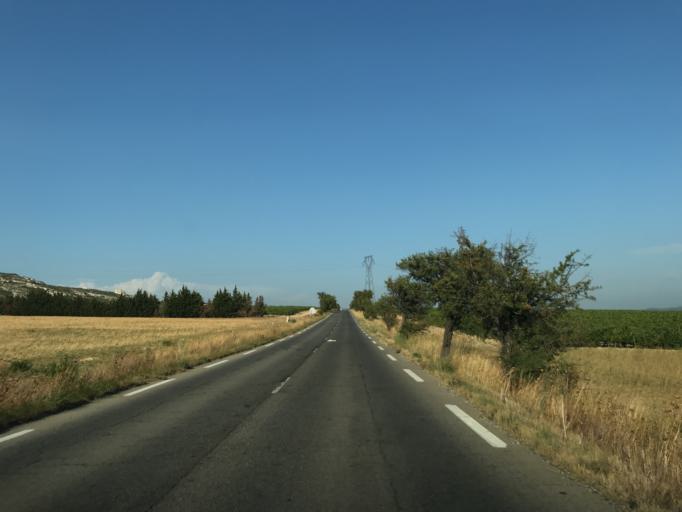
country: FR
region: Provence-Alpes-Cote d'Azur
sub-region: Departement des Bouches-du-Rhone
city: Cornillon-Confoux
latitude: 43.5357
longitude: 5.1160
